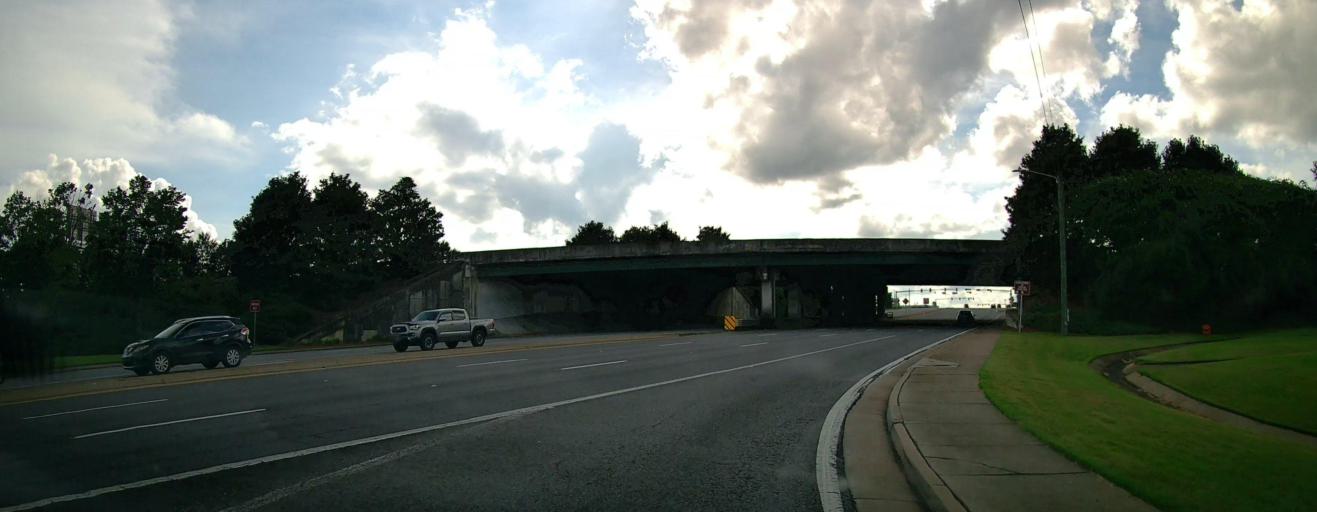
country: US
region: Georgia
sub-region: Muscogee County
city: Columbus
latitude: 32.5065
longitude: -84.9489
